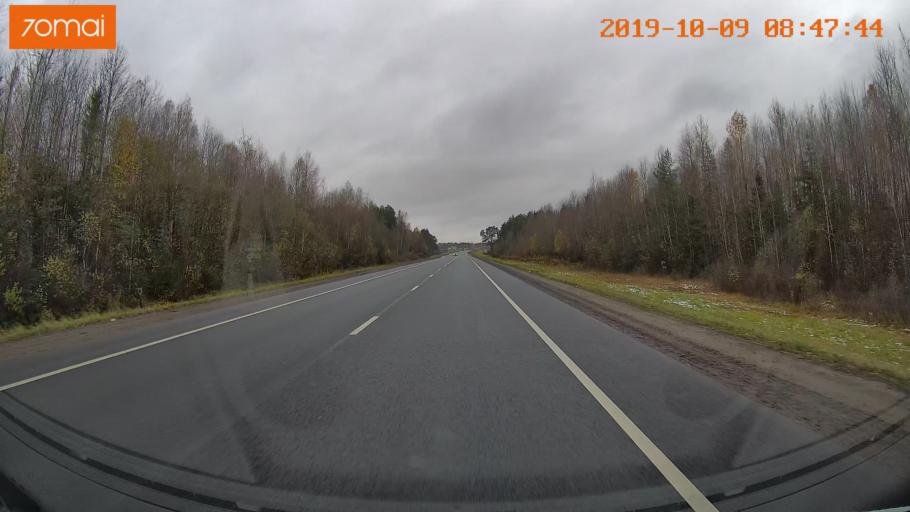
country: RU
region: Vologda
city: Vologda
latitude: 59.0675
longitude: 40.0399
